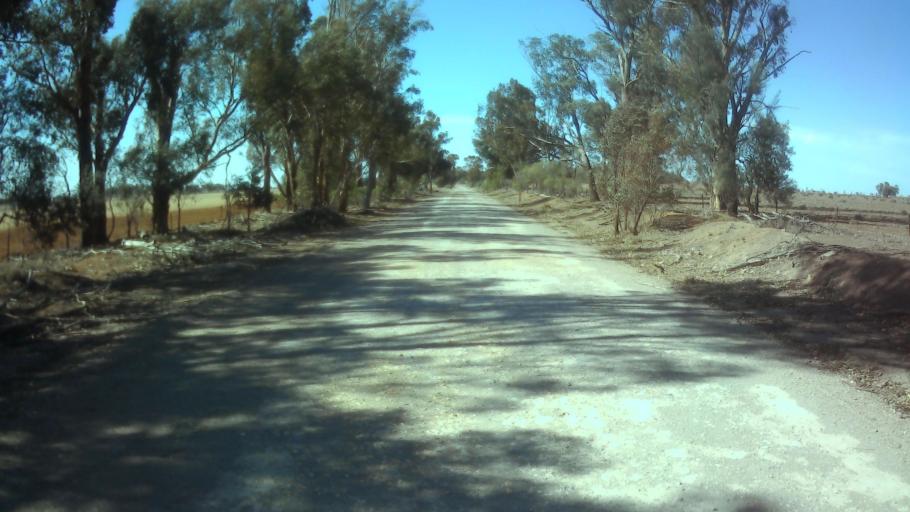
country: AU
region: New South Wales
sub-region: Forbes
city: Forbes
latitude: -33.7214
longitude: 147.7454
